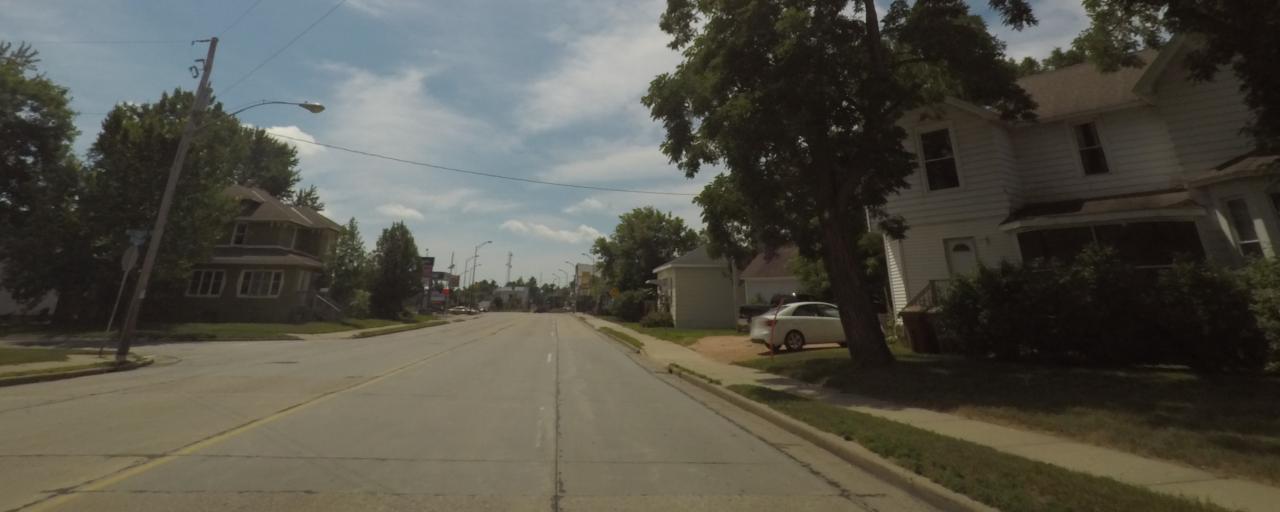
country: US
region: Wisconsin
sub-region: Portage County
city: Stevens Point
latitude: 44.5170
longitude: -89.5749
